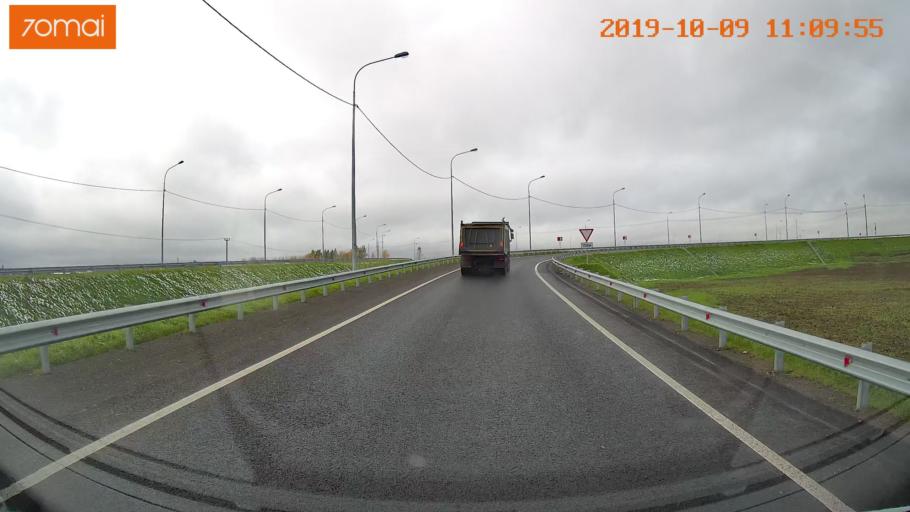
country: RU
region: Vologda
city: Vologda
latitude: 59.1572
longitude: 39.8137
